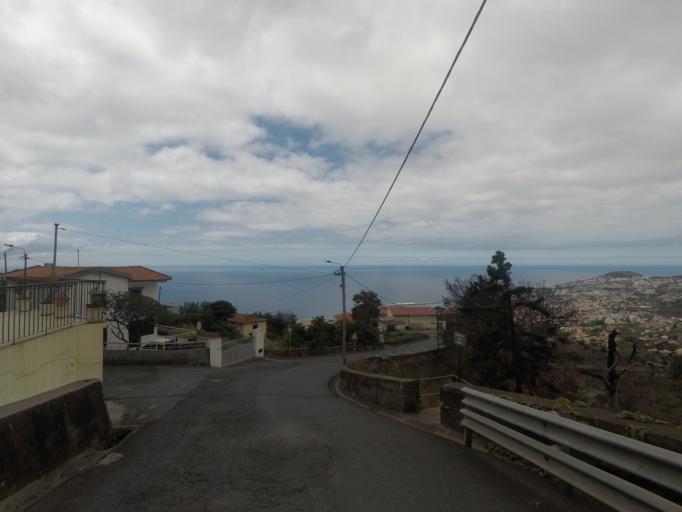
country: PT
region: Madeira
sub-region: Funchal
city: Nossa Senhora do Monte
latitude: 32.6655
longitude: -16.8940
